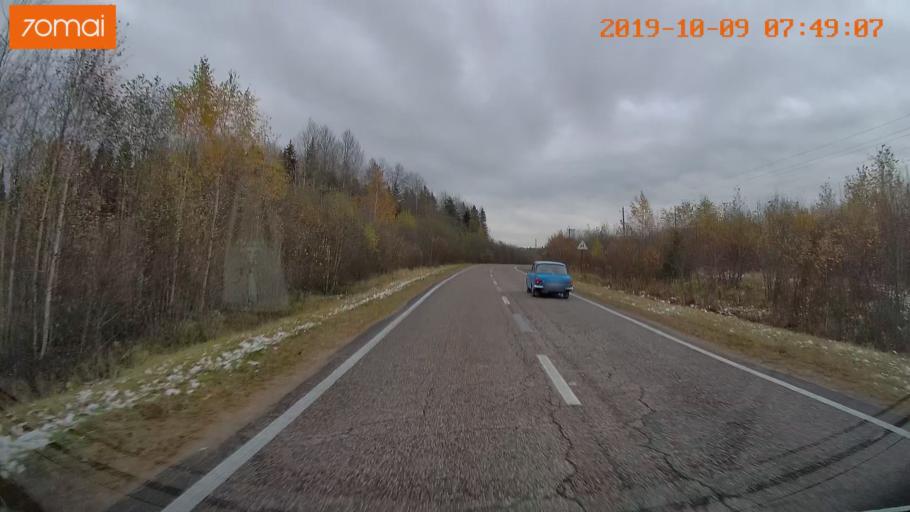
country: RU
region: Jaroslavl
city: Kukoboy
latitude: 58.6677
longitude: 39.8406
